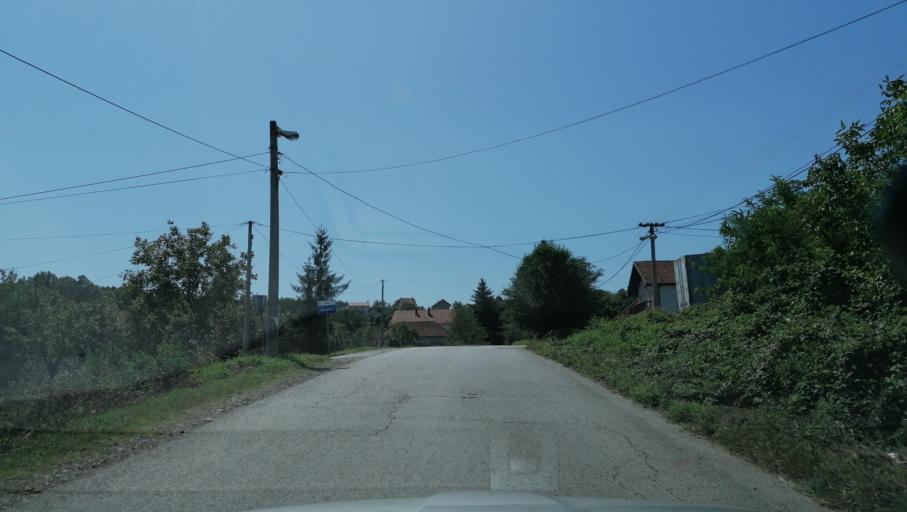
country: RS
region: Central Serbia
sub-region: Kolubarski Okrug
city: Valjevo
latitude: 44.2556
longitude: 19.8765
